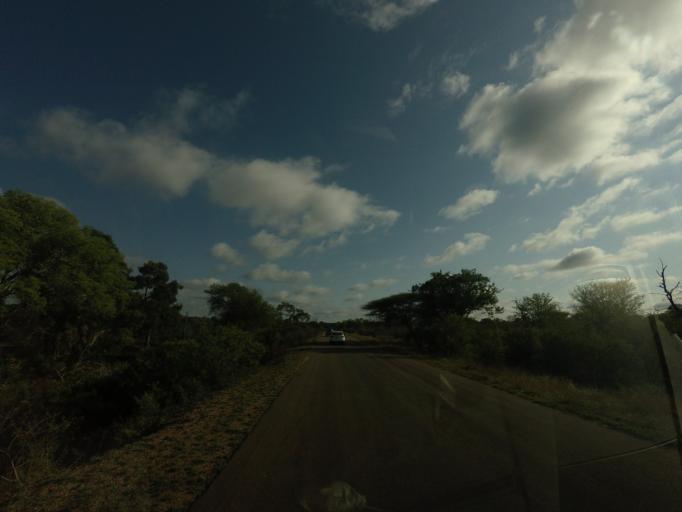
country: ZA
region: Mpumalanga
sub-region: Ehlanzeni District
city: Komatipoort
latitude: -25.2500
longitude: 31.8479
